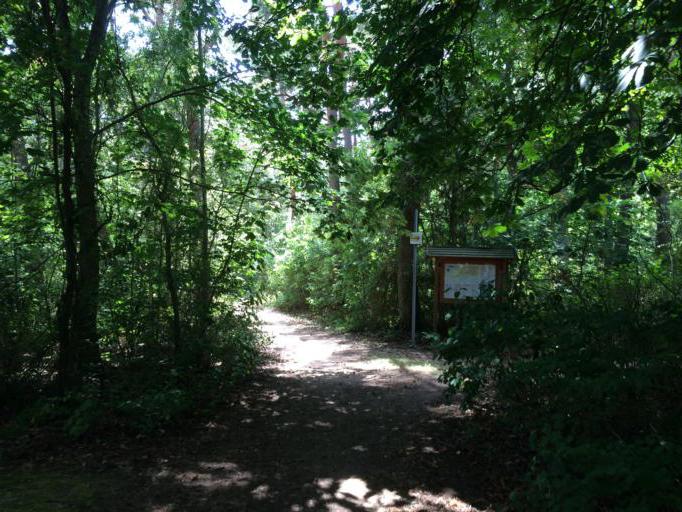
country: SE
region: Skane
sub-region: Vellinge Kommun
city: Skanor med Falsterbo
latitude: 55.3923
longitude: 12.8421
